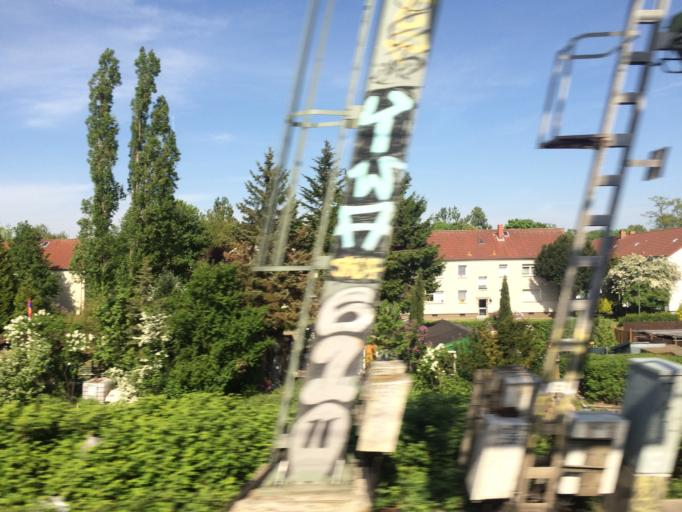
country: DE
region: North Rhine-Westphalia
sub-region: Regierungsbezirk Dusseldorf
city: Erkrath
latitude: 51.1736
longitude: 6.8675
